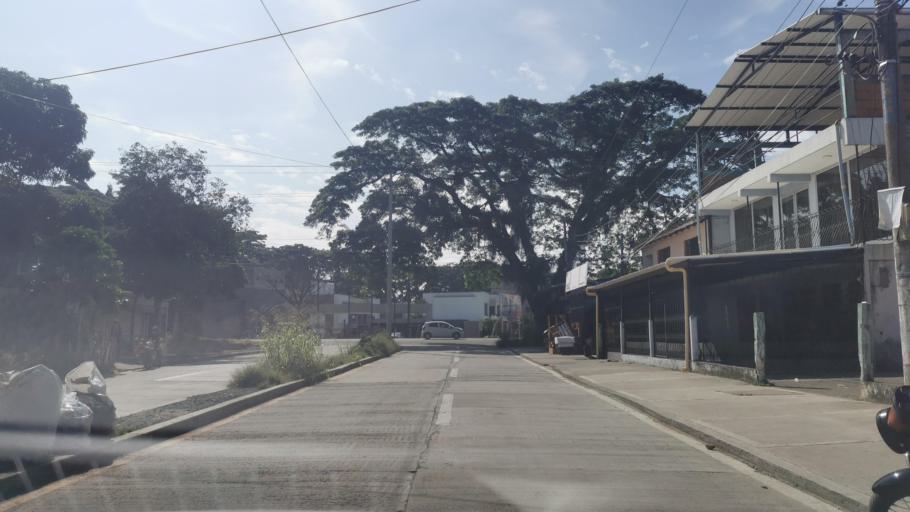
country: CO
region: Valle del Cauca
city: Jamundi
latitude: 3.2675
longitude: -76.5333
